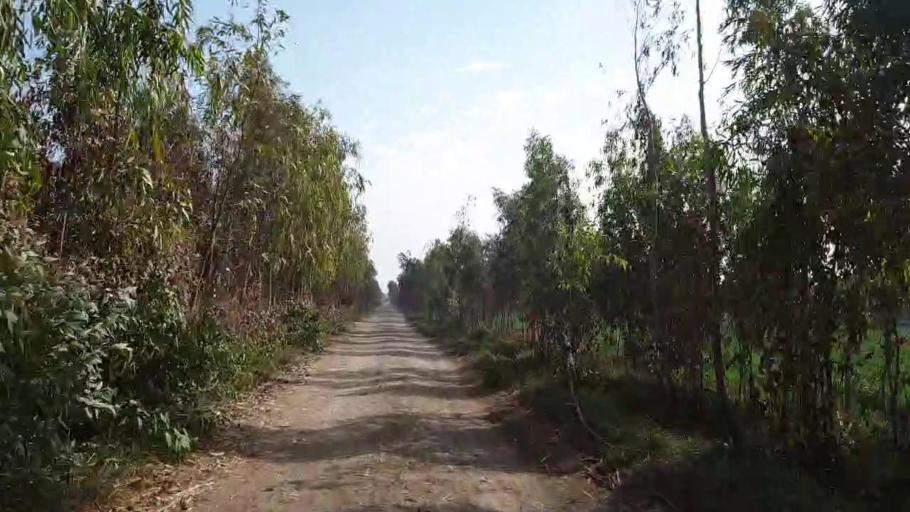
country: PK
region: Sindh
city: Matiari
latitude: 25.6002
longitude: 68.4986
